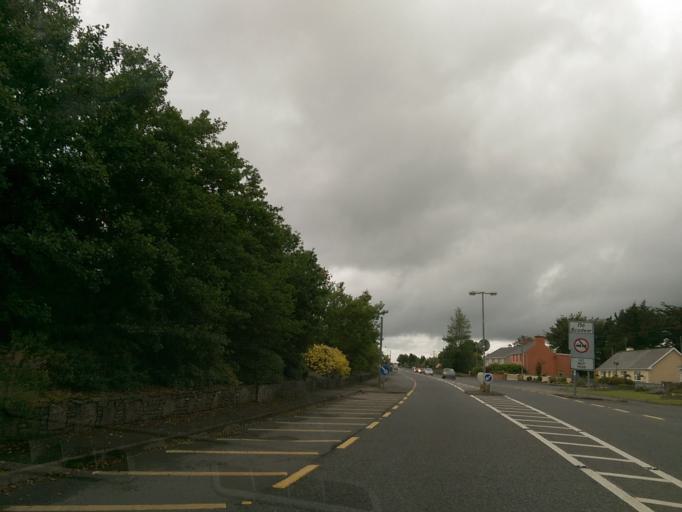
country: IE
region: Munster
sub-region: An Clar
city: Ennis
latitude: 52.7502
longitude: -9.1448
